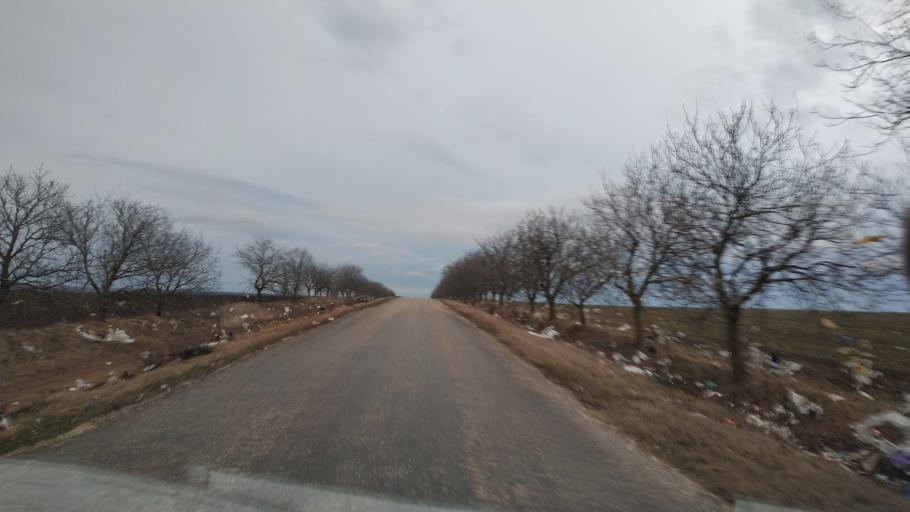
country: MD
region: Causeni
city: Causeni
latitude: 46.5885
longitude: 29.3944
